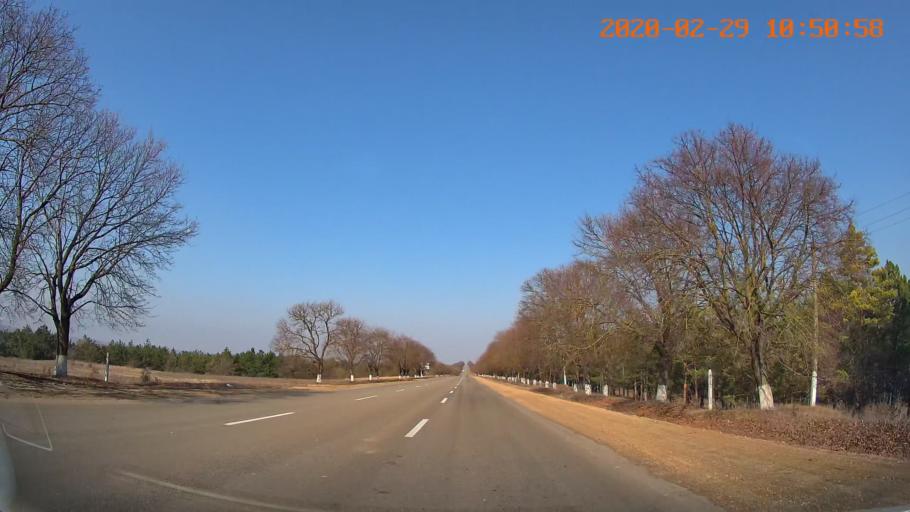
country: MD
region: Telenesti
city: Grigoriopol
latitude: 47.0884
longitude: 29.3702
